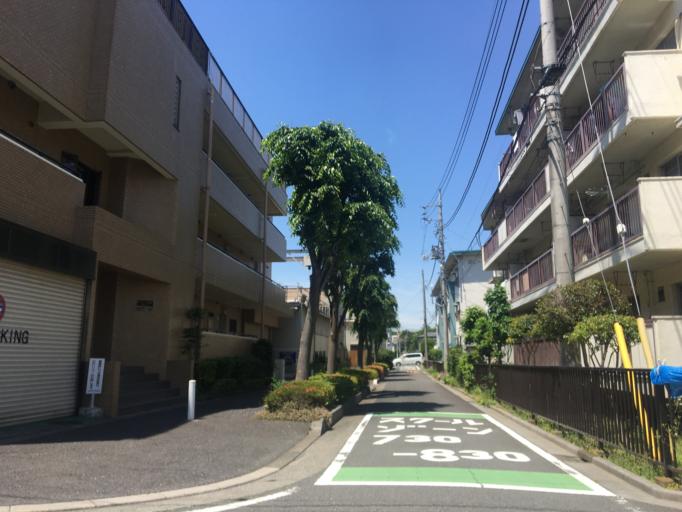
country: JP
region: Saitama
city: Yono
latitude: 35.8653
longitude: 139.6431
